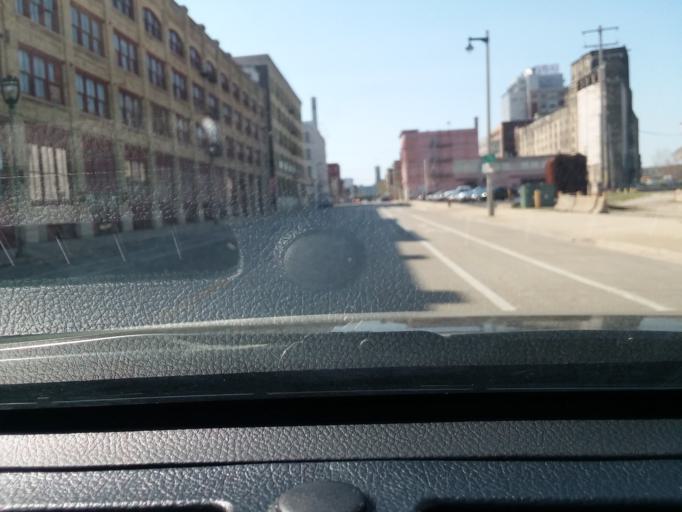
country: US
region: Wisconsin
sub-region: Milwaukee County
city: Milwaukee
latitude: 43.0317
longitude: -87.9126
